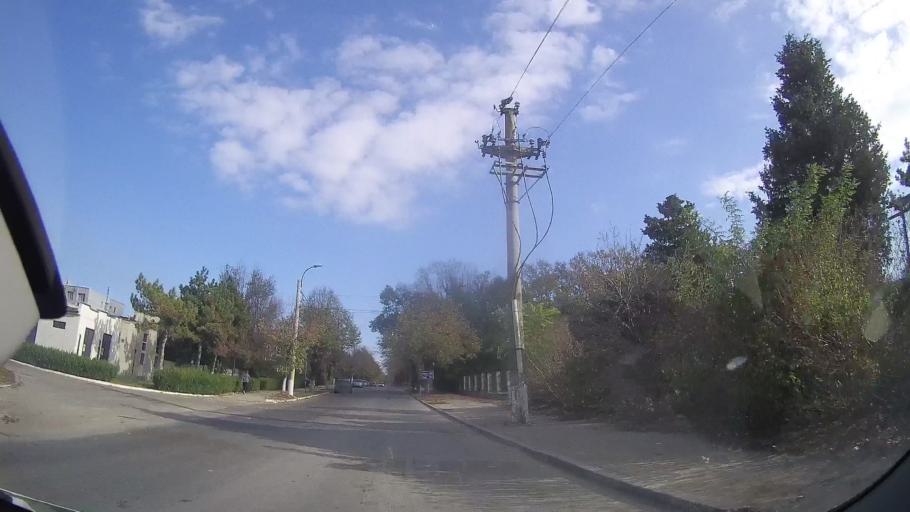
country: RO
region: Constanta
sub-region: Oras Eforie
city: Eforie Nord
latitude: 44.0600
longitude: 28.6250
